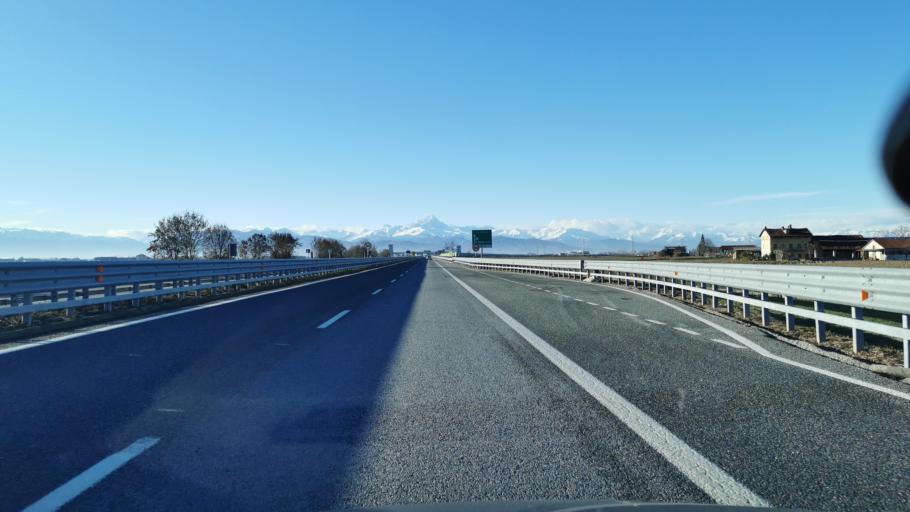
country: IT
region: Piedmont
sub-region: Provincia di Cuneo
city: Sant'Albano Stura
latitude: 44.4727
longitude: 7.7063
